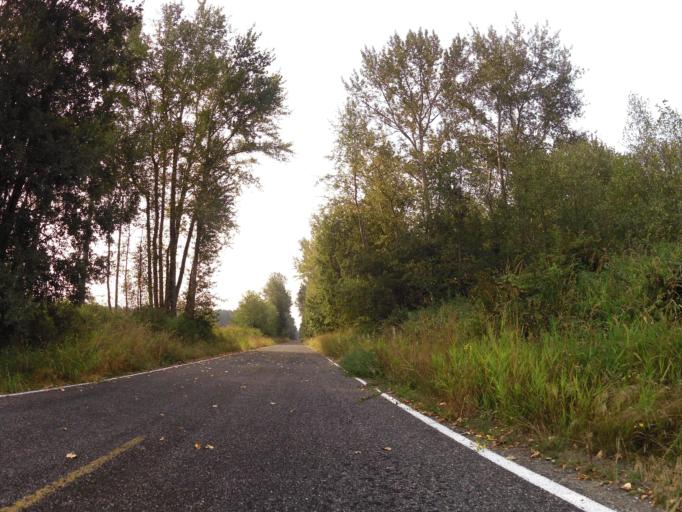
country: US
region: Washington
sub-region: Whatcom County
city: Birch Bay
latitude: 48.8745
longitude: -122.7317
